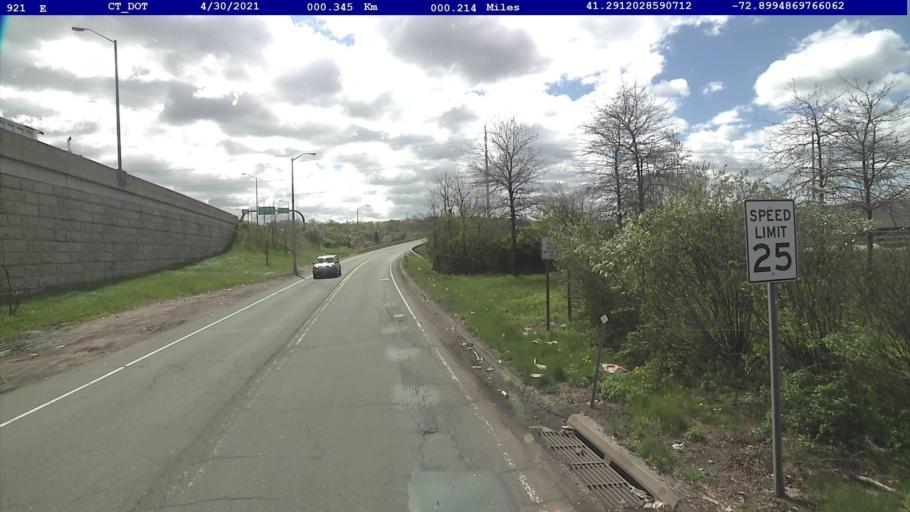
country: US
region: Connecticut
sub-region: New Haven County
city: New Haven
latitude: 41.2910
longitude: -72.9000
